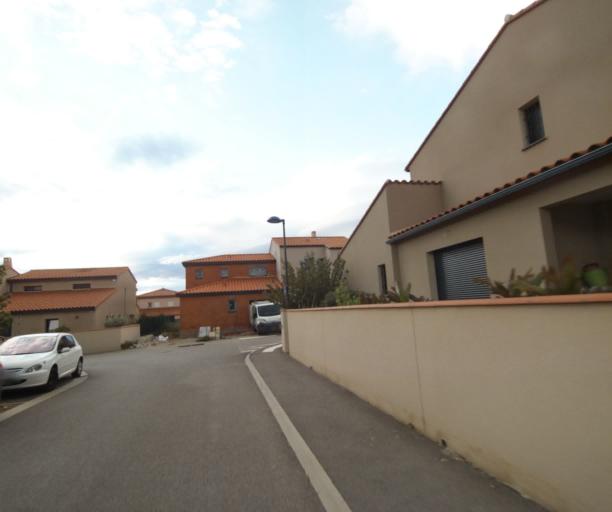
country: FR
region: Languedoc-Roussillon
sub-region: Departement des Pyrenees-Orientales
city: Argelers
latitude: 42.5554
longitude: 3.0226
